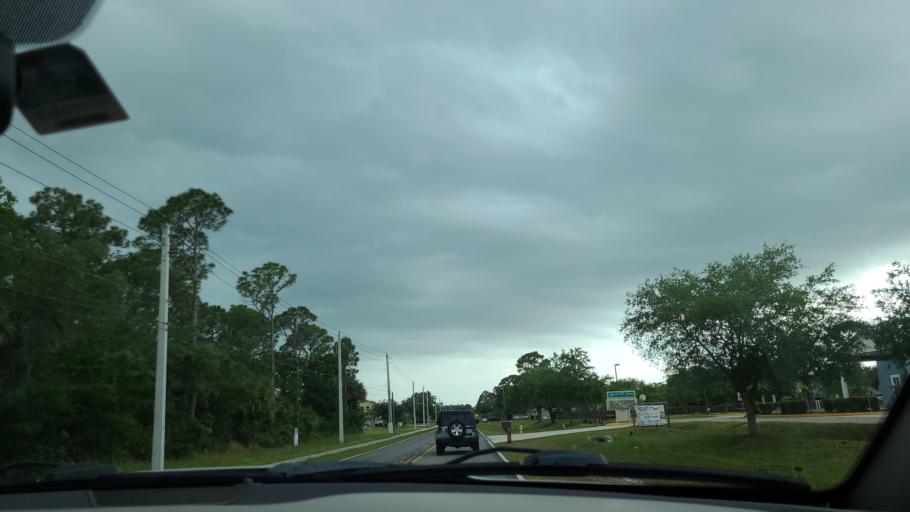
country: US
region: Florida
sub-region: Brevard County
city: June Park
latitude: 28.0111
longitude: -80.6796
